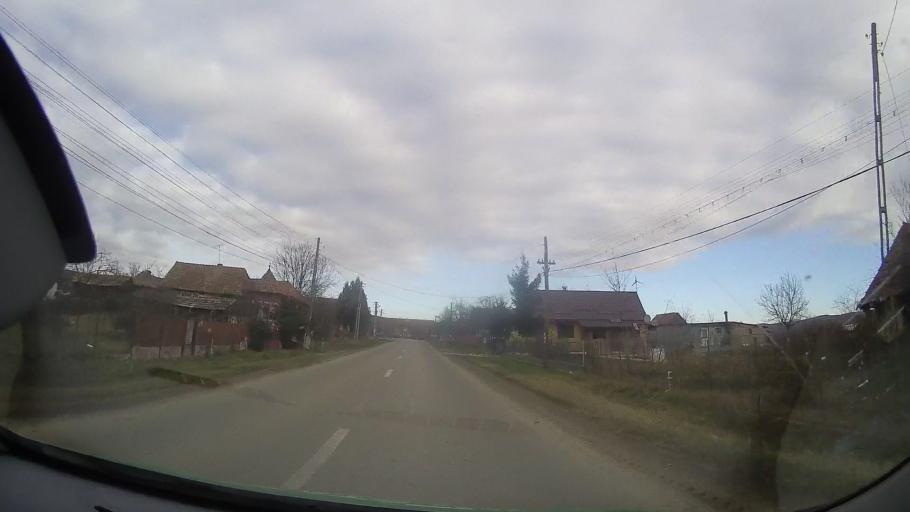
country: RO
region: Mures
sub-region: Comuna Iernut
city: Iernut
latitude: 46.4754
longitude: 24.2275
